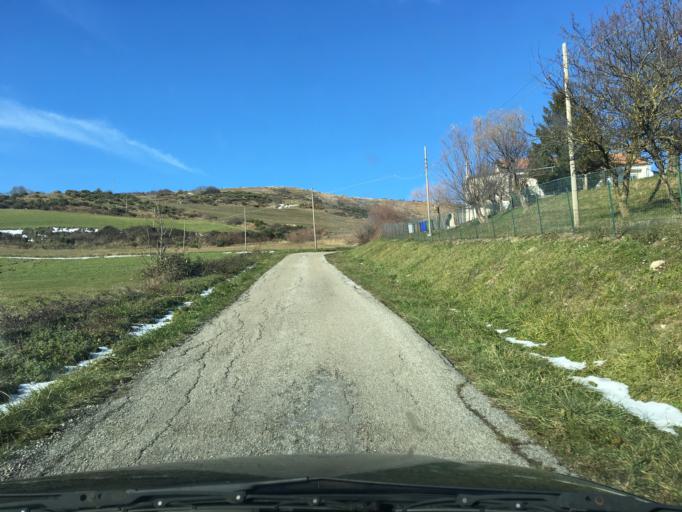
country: IT
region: Molise
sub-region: Provincia di Isernia
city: Agnone
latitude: 41.8468
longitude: 14.3527
